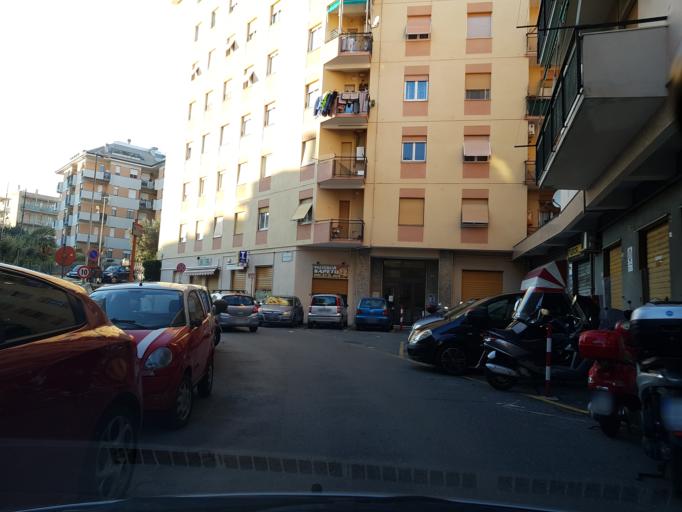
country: IT
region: Liguria
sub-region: Provincia di Genova
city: Genoa
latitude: 44.4090
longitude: 8.9824
